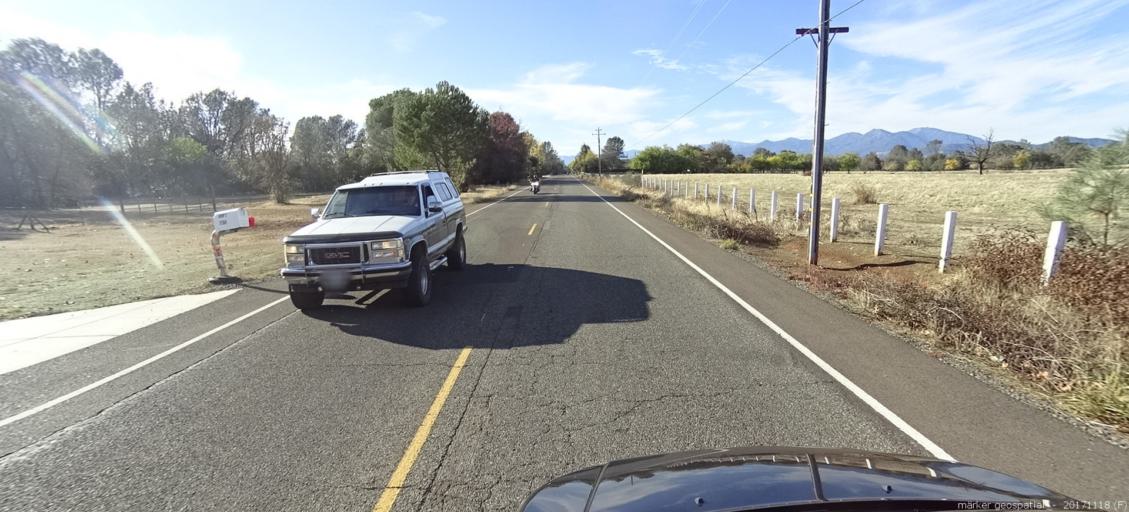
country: US
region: California
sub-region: Shasta County
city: Redding
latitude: 40.4779
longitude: -122.4135
